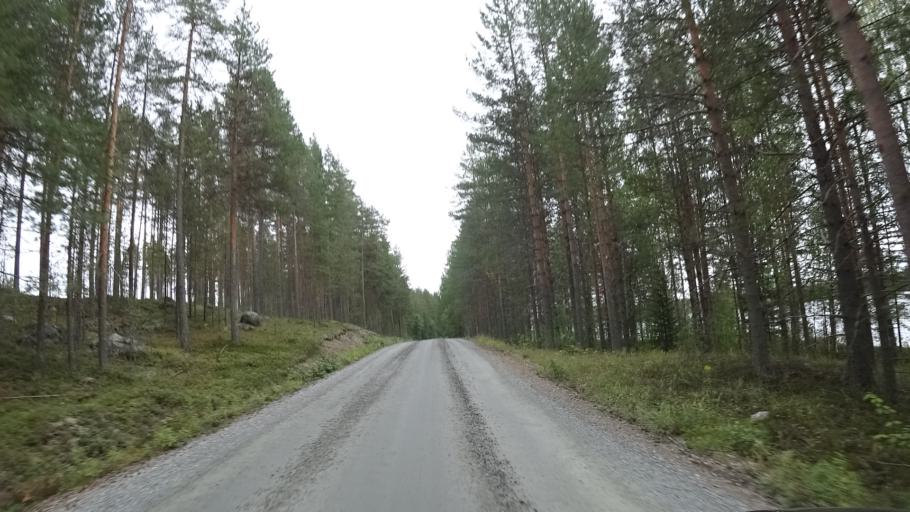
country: FI
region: North Karelia
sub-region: Pielisen Karjala
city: Lieksa
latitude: 63.3839
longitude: 30.3400
